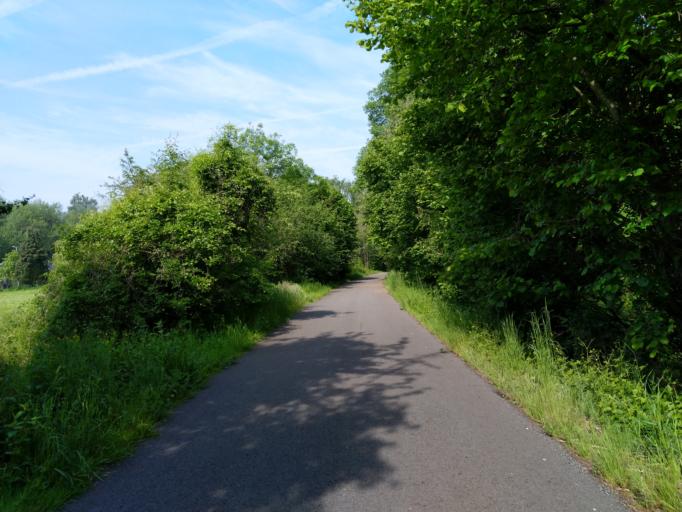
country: BE
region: Wallonia
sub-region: Province du Hainaut
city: Colfontaine
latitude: 50.4206
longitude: 3.8572
